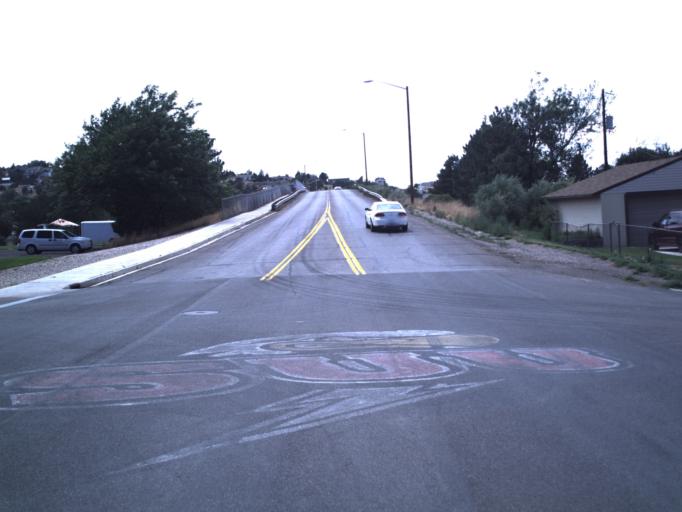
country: US
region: Utah
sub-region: Iron County
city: Cedar City
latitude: 37.6770
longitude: -113.0776
